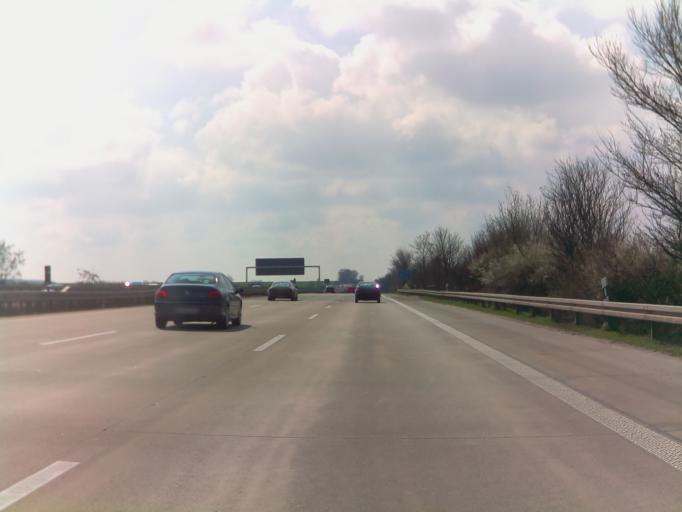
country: DE
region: Saxony-Anhalt
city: Osterfeld
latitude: 51.0858
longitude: 11.9554
